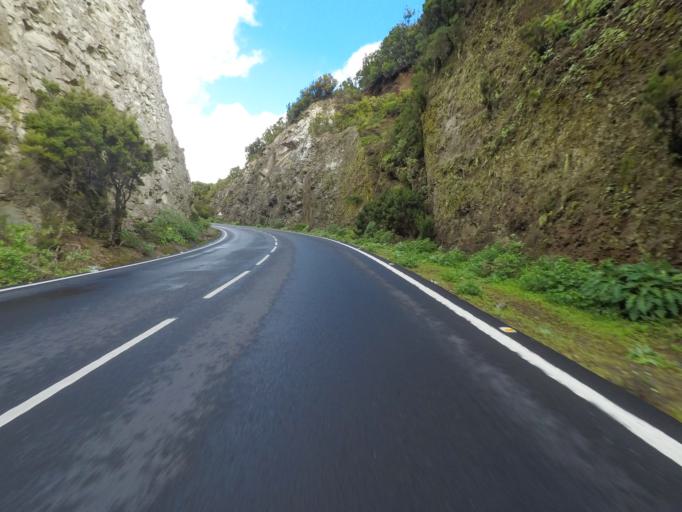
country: ES
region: Canary Islands
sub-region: Provincia de Santa Cruz de Tenerife
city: Alajero
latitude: 28.1107
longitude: -17.2172
